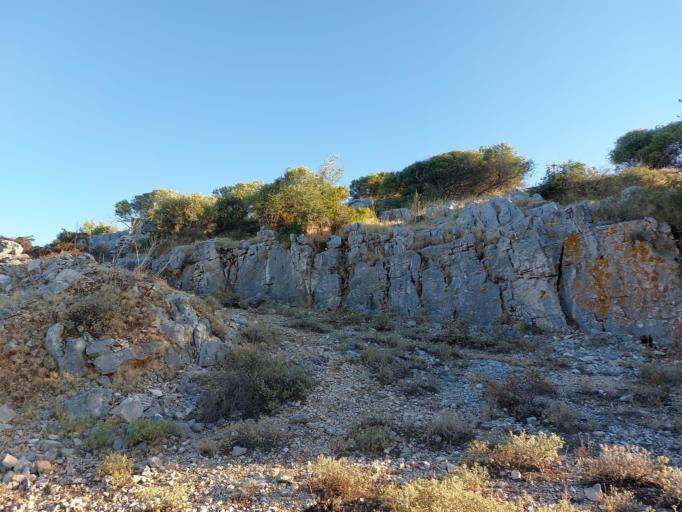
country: HR
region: Dubrovacko-Neretvanska
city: Smokvica
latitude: 42.7286
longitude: 16.8411
